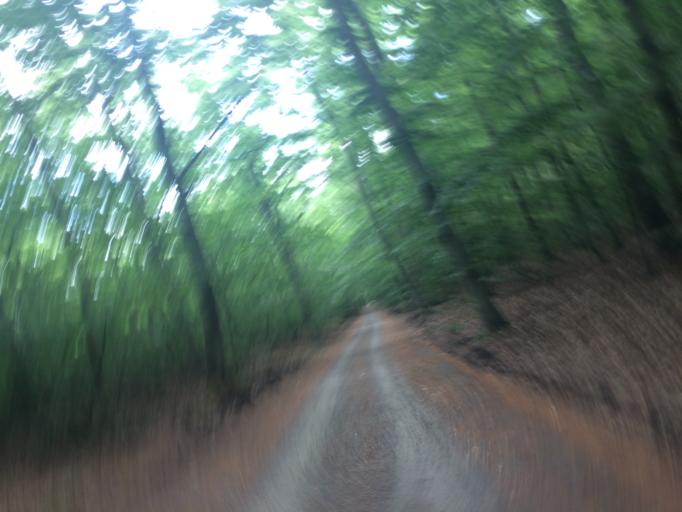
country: DK
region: Capital Region
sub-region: Bornholm Kommune
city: Ronne
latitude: 55.1357
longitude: 14.7163
